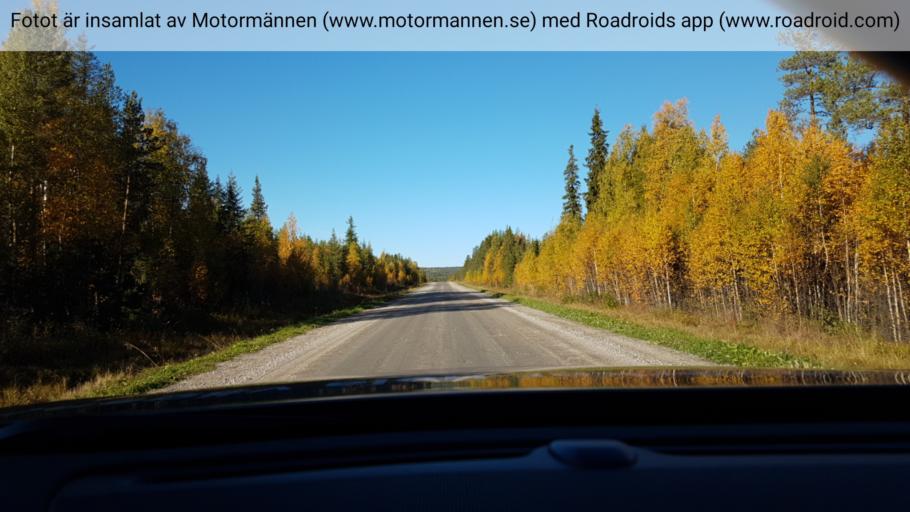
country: SE
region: Norrbotten
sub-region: Alvsbyns Kommun
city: AElvsbyn
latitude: 66.2651
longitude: 21.0337
